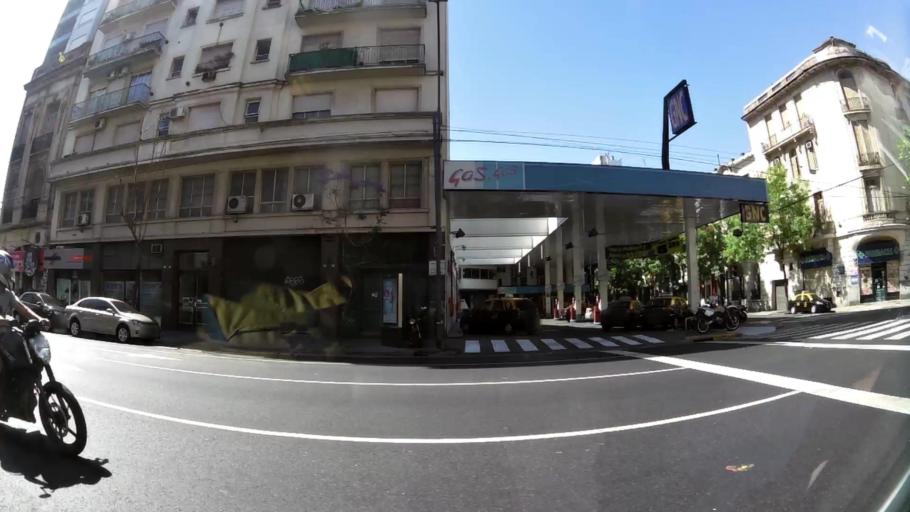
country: AR
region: Buenos Aires F.D.
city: Buenos Aires
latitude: -34.6224
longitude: -58.3859
